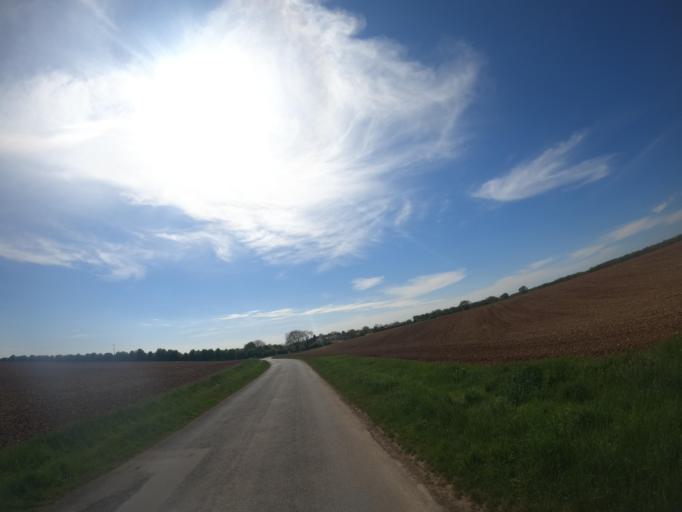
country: FR
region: Poitou-Charentes
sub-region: Departement des Deux-Sevres
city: Airvault
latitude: 46.8868
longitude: -0.1291
